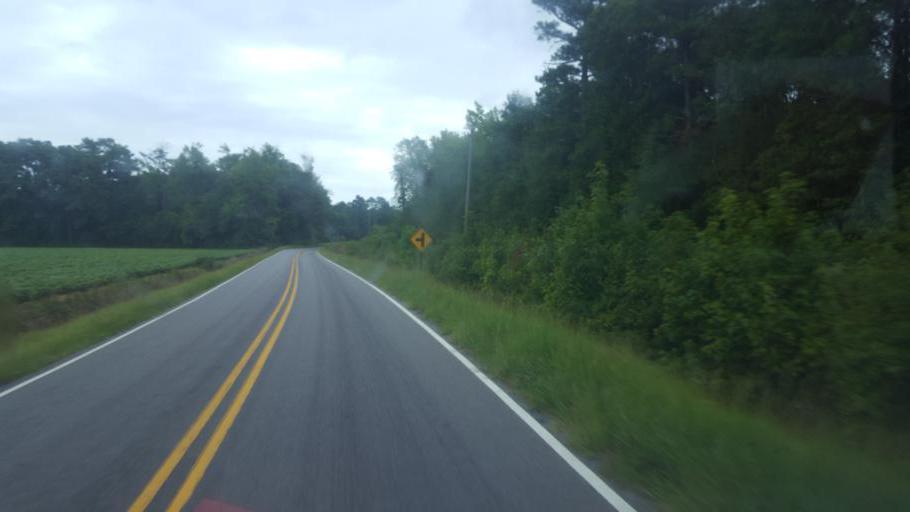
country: US
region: North Carolina
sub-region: Tyrrell County
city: Columbia
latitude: 35.9461
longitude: -76.2932
